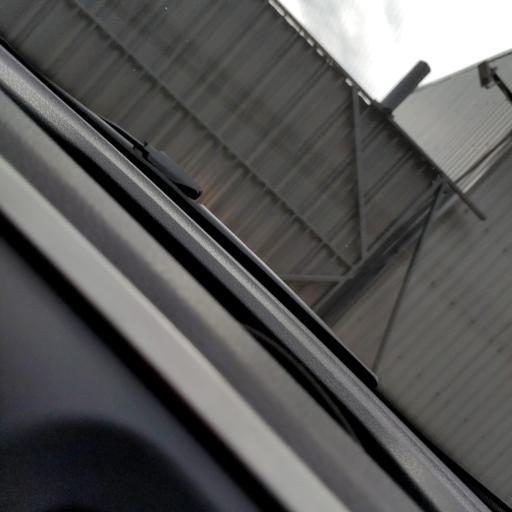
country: RU
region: Samara
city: Tol'yatti
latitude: 53.5332
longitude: 49.2553
